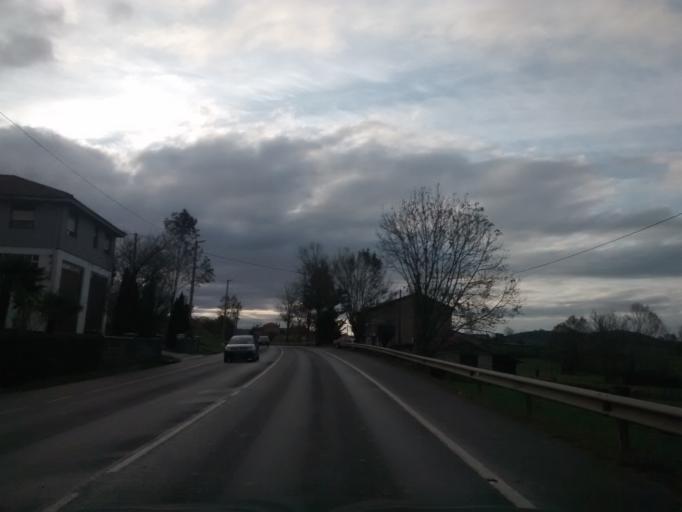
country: ES
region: Cantabria
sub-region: Provincia de Cantabria
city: Penagos
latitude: 43.3409
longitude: -3.8129
